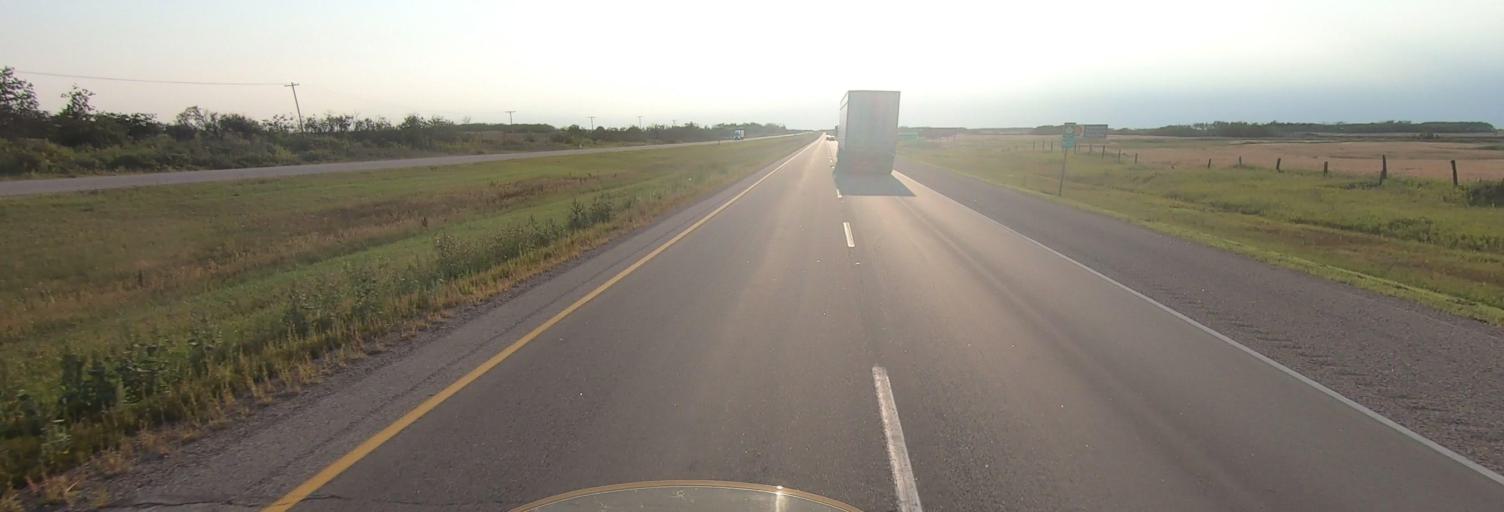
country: CA
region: Saskatchewan
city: White City
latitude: 50.5145
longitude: -104.0718
